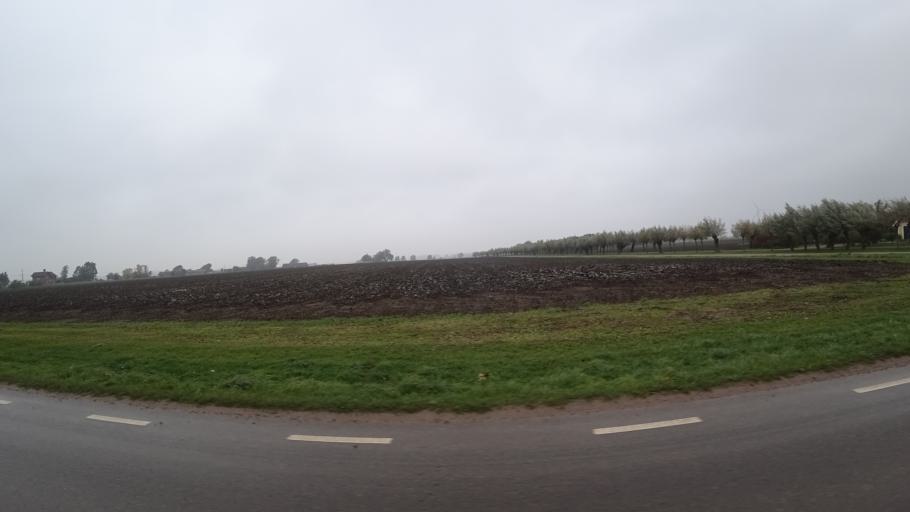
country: SE
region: Skane
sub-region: Kavlinge Kommun
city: Kaevlinge
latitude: 55.8212
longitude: 13.1122
